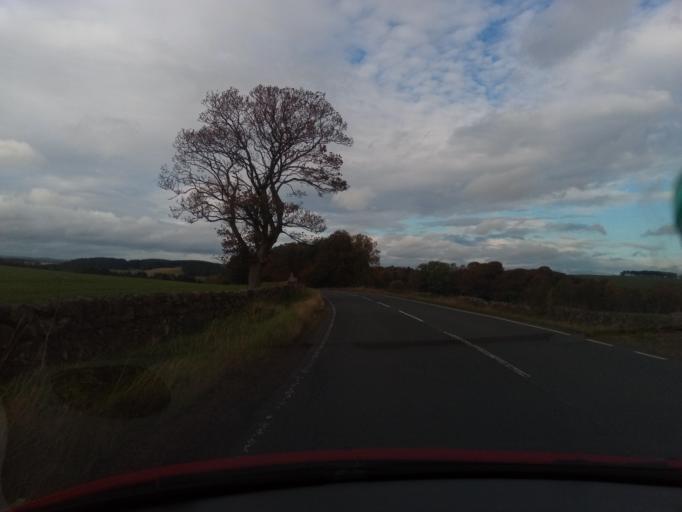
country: GB
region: Scotland
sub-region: South Lanarkshire
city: Biggar
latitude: 55.6814
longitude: -3.5350
